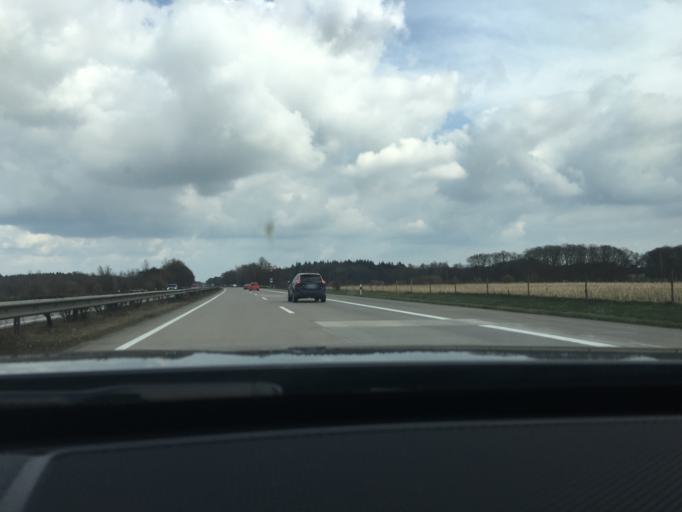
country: DE
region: Lower Saxony
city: Wildeshausen
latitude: 52.9256
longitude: 8.4898
